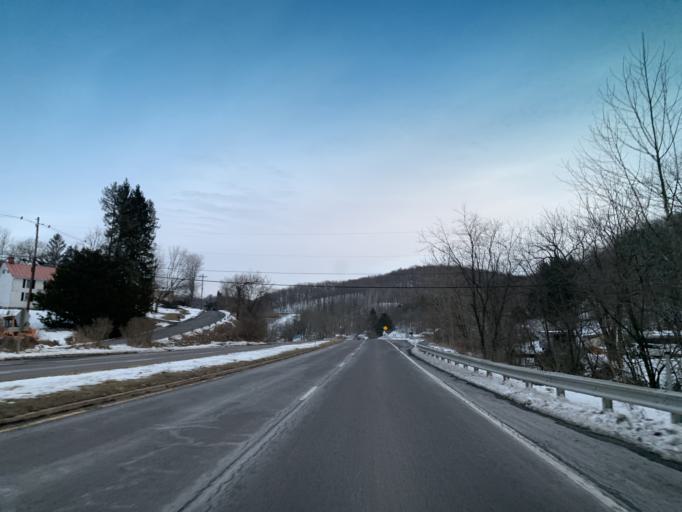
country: US
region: Maryland
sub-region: Allegany County
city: Cumberland
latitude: 39.6778
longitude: -78.6980
